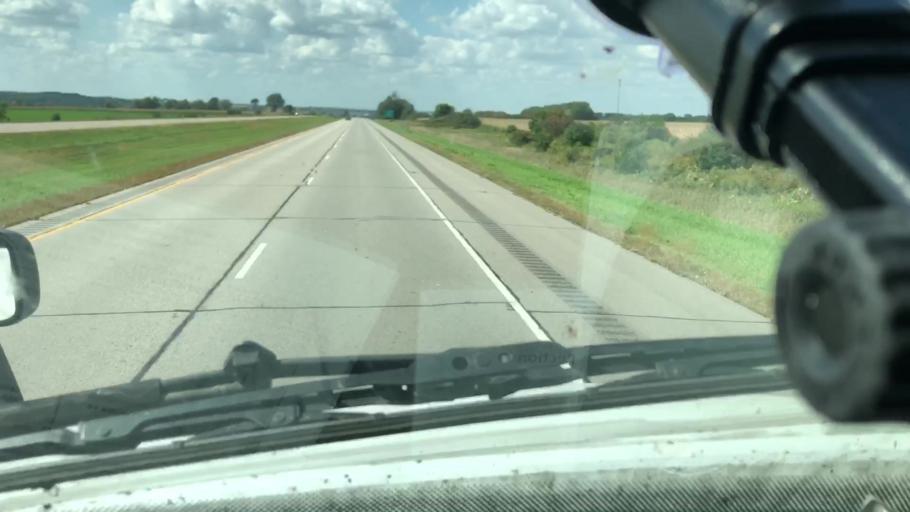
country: US
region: Minnesota
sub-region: Olmsted County
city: Eyota
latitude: 43.9560
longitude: -92.3279
